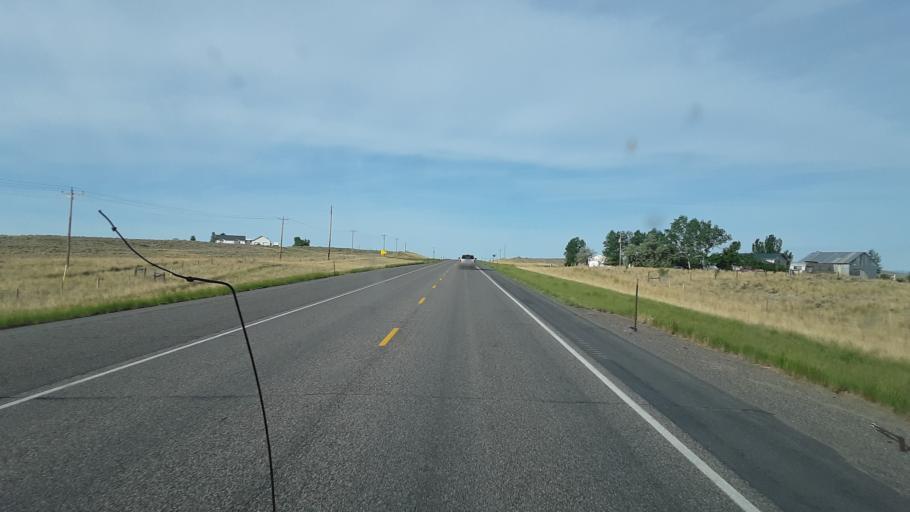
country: US
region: Wyoming
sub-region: Fremont County
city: Riverton
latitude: 43.1649
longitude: -108.2650
